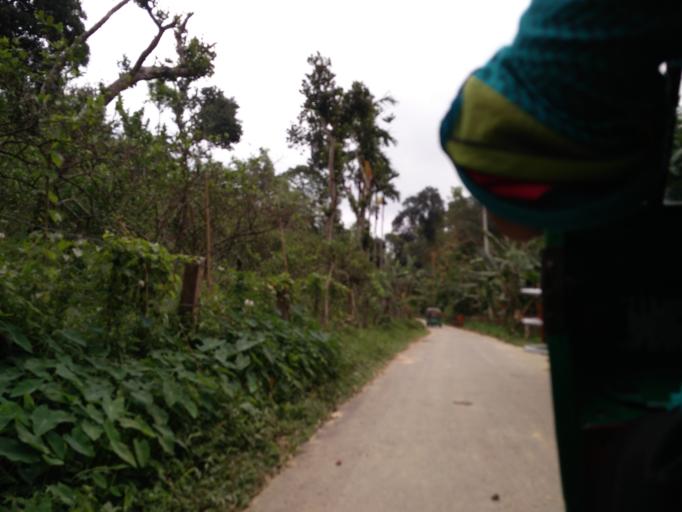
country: IN
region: Tripura
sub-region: Dhalai
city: Kamalpur
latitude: 24.3021
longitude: 91.7823
